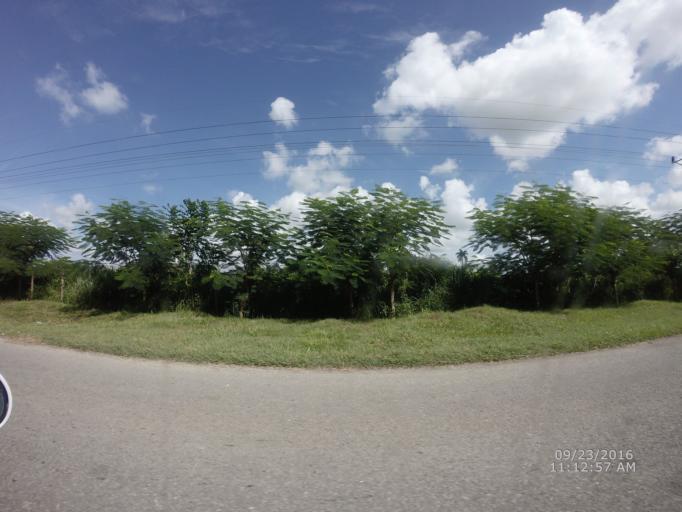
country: CU
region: La Habana
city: Arroyo Naranjo
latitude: 23.0304
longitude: -82.2910
